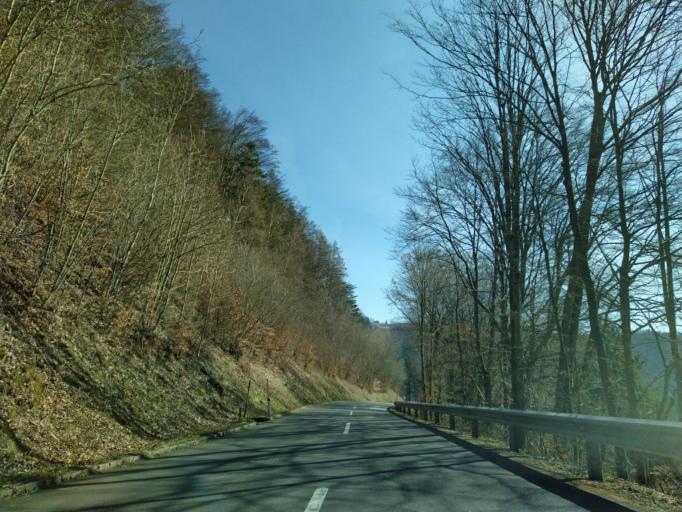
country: AT
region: Upper Austria
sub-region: Politischer Bezirk Urfahr-Umgebung
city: Kirchschlag bei Linz
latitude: 48.3863
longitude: 14.2885
